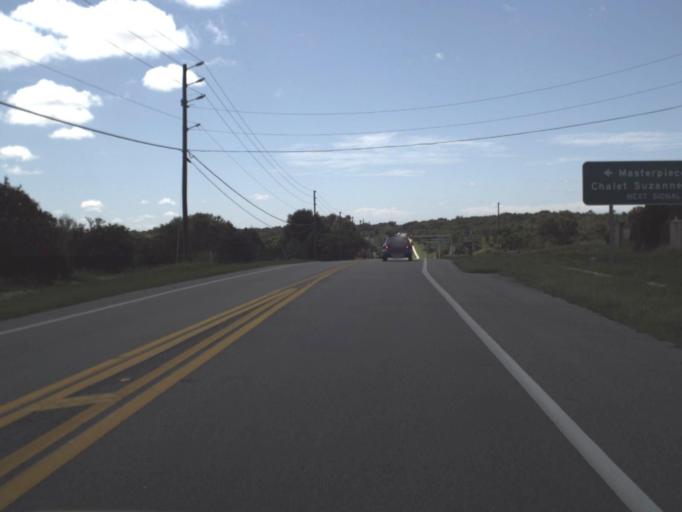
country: US
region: Florida
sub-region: Polk County
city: Lake Wales
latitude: 27.9627
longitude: -81.5948
